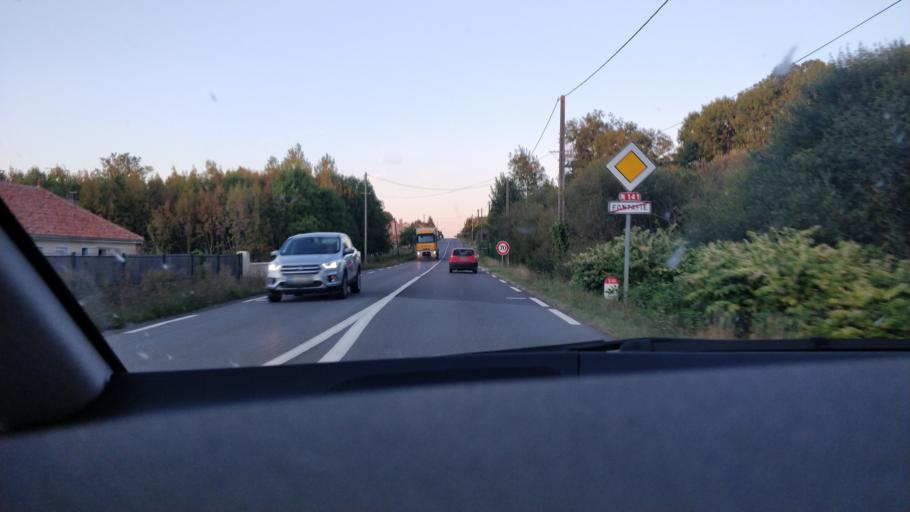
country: FR
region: Poitou-Charentes
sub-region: Departement de la Charente
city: Loubert
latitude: 45.8680
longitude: 0.5455
